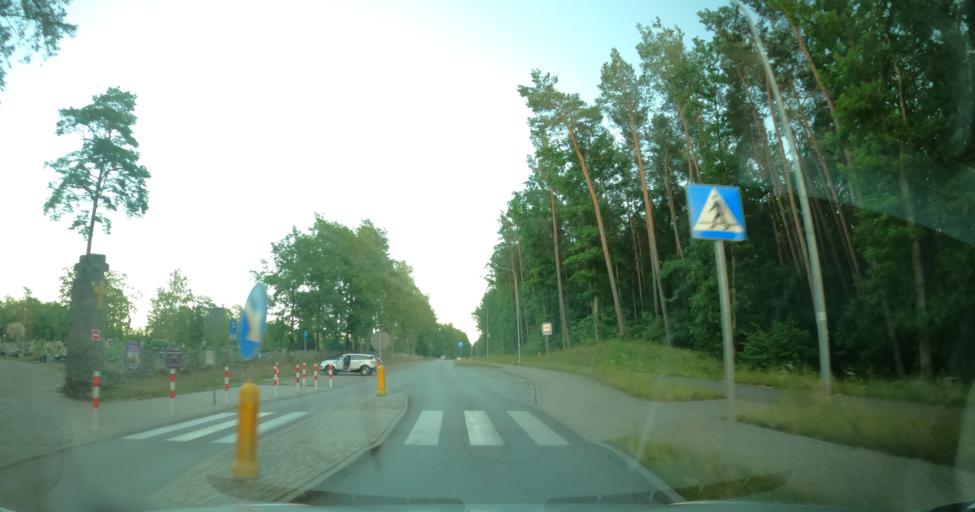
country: PL
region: Pomeranian Voivodeship
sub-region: Powiat leborski
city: Lebork
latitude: 54.5254
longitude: 17.7751
